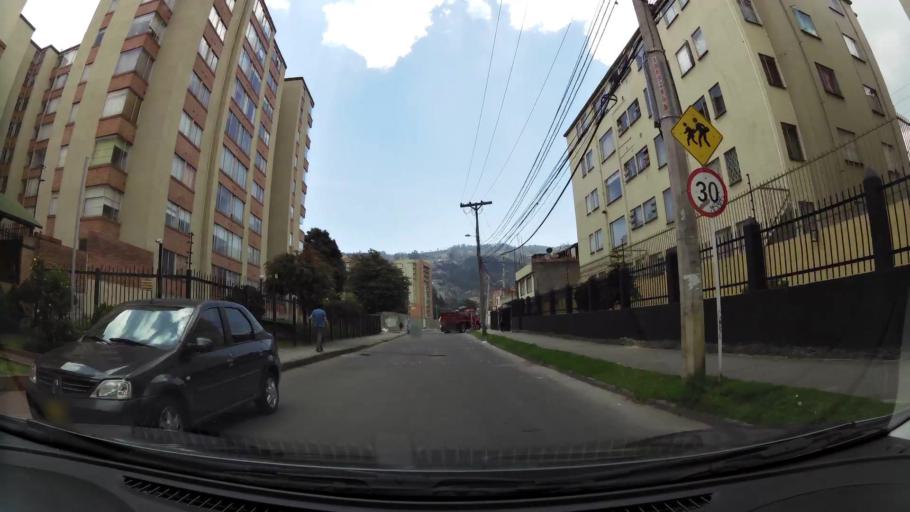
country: CO
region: Cundinamarca
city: La Calera
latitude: 4.7441
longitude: -74.0302
